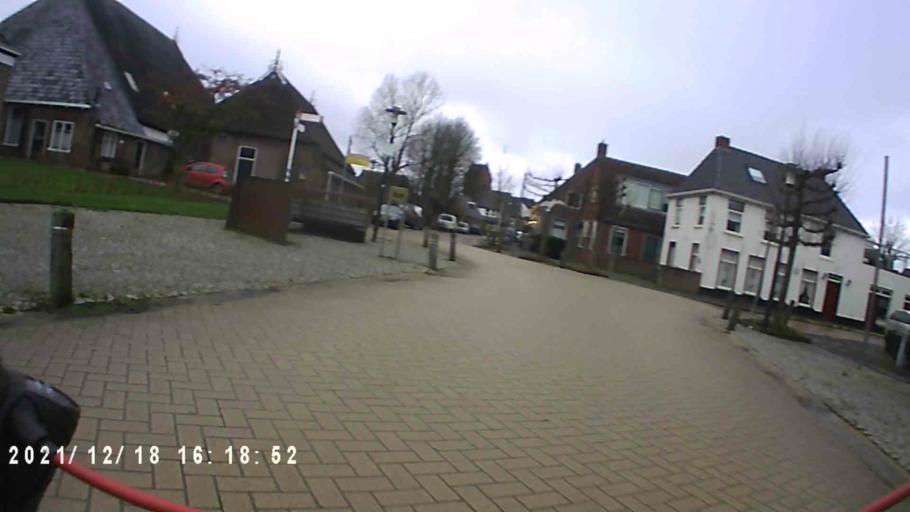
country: NL
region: Friesland
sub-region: Gemeente Dongeradeel
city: Anjum
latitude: 53.3774
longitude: 6.0552
